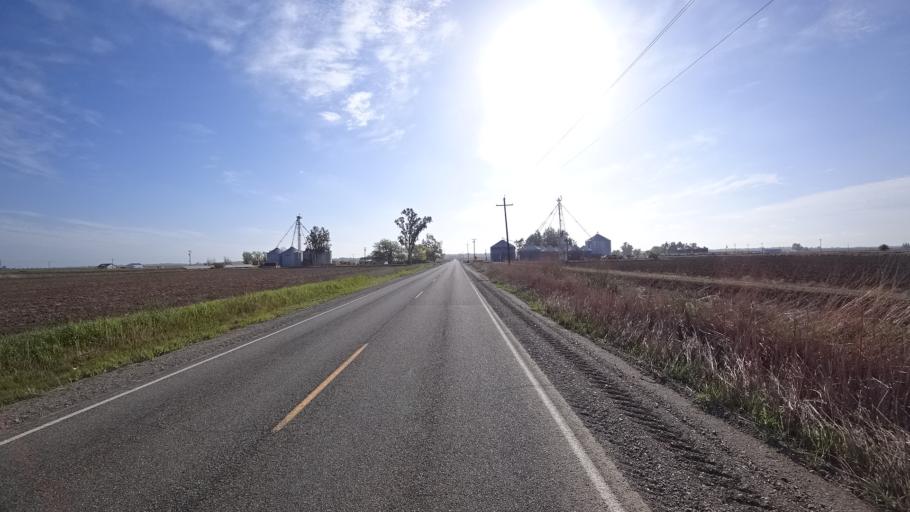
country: US
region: California
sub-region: Glenn County
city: Hamilton City
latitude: 39.5824
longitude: -122.0303
